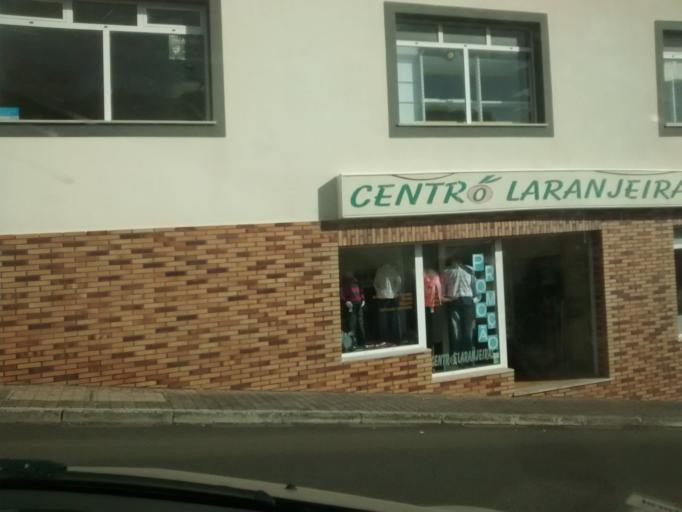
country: PT
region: Madeira
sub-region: Calheta
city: Estreito da Calheta
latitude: 32.7315
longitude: -17.1763
